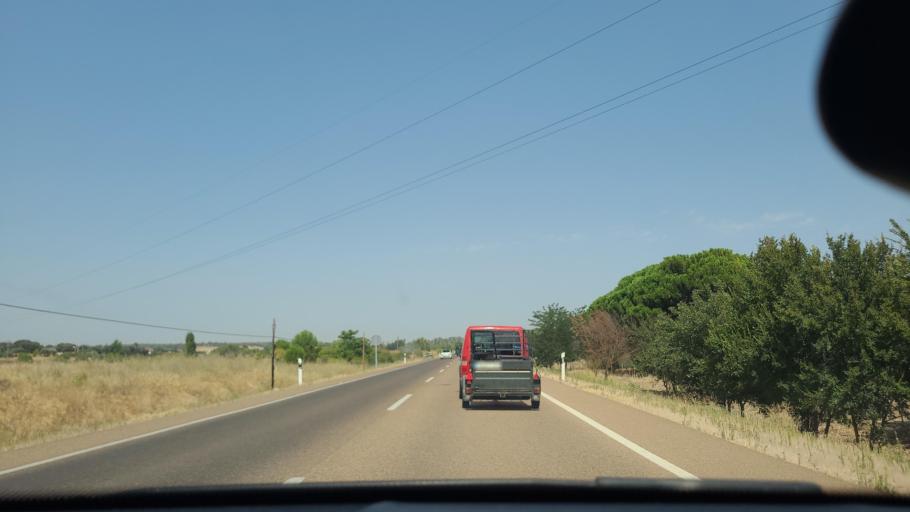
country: ES
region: Extremadura
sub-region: Provincia de Badajoz
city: Badajoz
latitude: 38.8270
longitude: -6.9137
